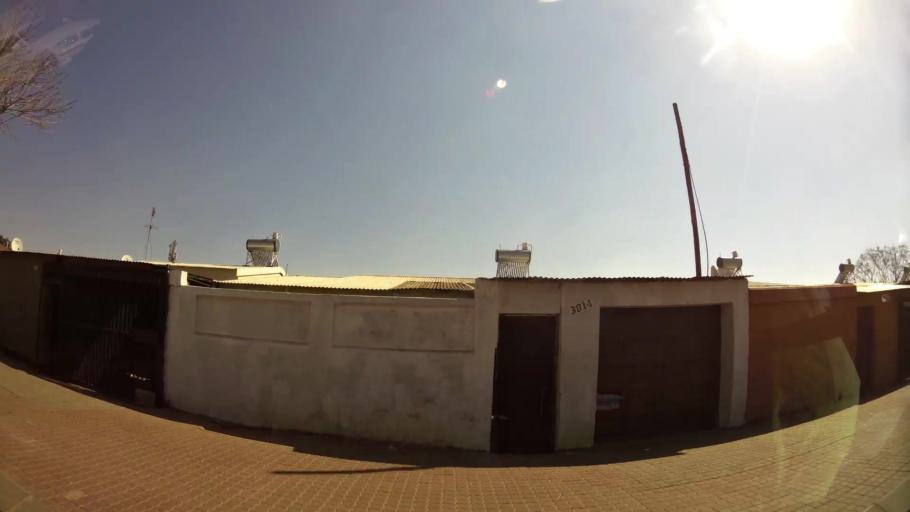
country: ZA
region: Gauteng
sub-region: City of Johannesburg Metropolitan Municipality
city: Johannesburg
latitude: -26.1833
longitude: 27.9755
